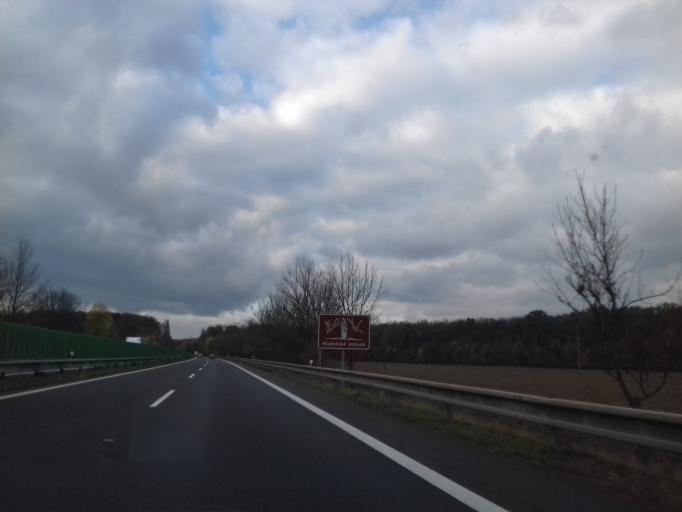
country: CZ
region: Olomoucky
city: Litovel
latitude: 49.7013
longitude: 17.0377
